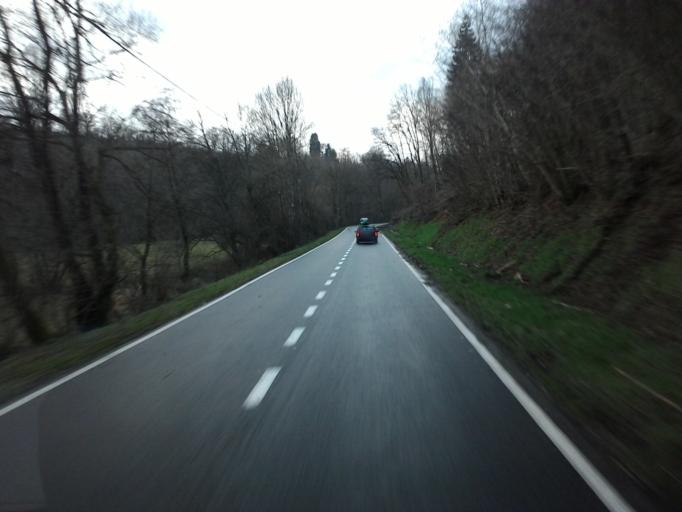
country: BE
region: Wallonia
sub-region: Province de Liege
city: Stoumont
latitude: 50.3793
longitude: 5.7464
